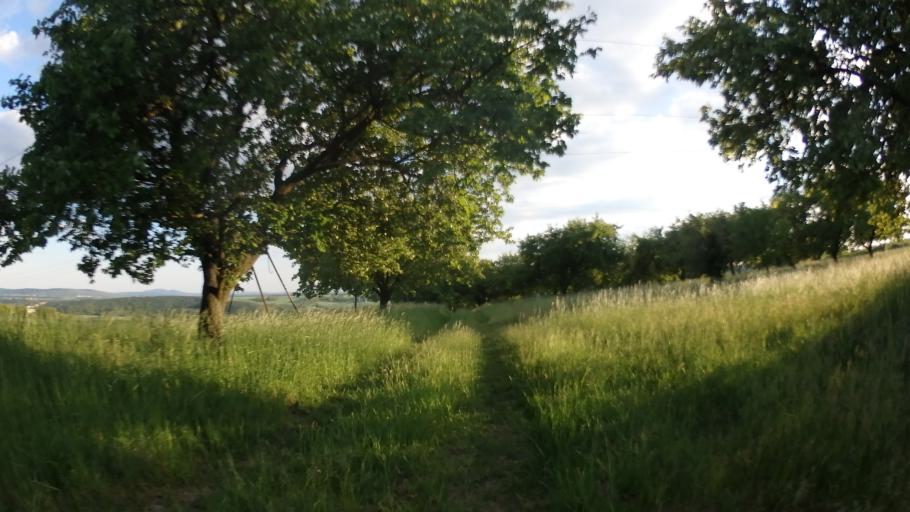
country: CZ
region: South Moravian
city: Zelesice
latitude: 49.1280
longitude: 16.5838
